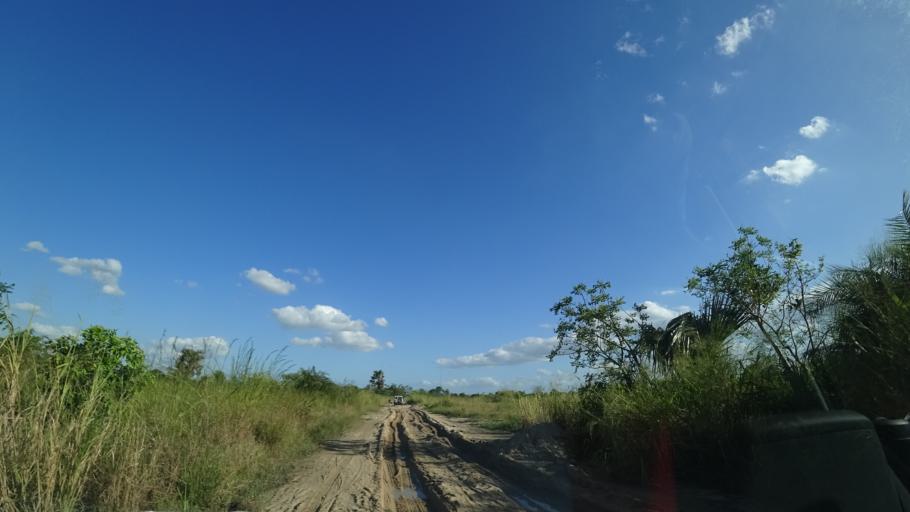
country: MZ
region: Sofala
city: Dondo
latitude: -19.3725
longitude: 34.5924
